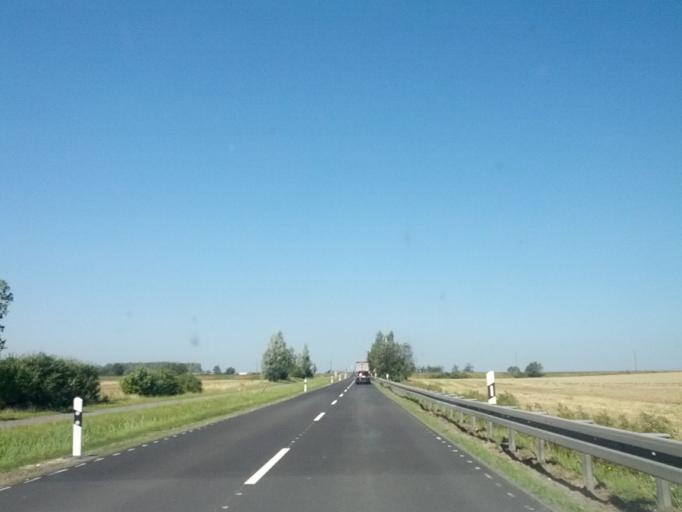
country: DE
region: Mecklenburg-Vorpommern
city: Sagard
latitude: 54.5070
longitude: 13.5425
